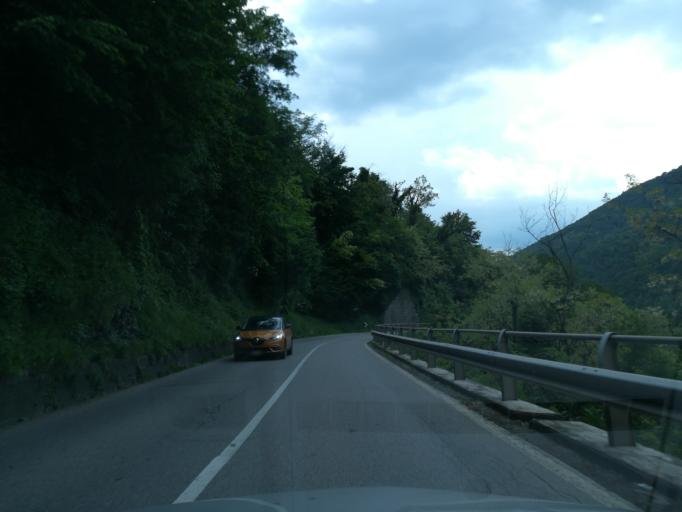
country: IT
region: Lombardy
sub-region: Provincia di Bergamo
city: Almenno San Salvatore
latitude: 45.7594
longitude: 9.5953
